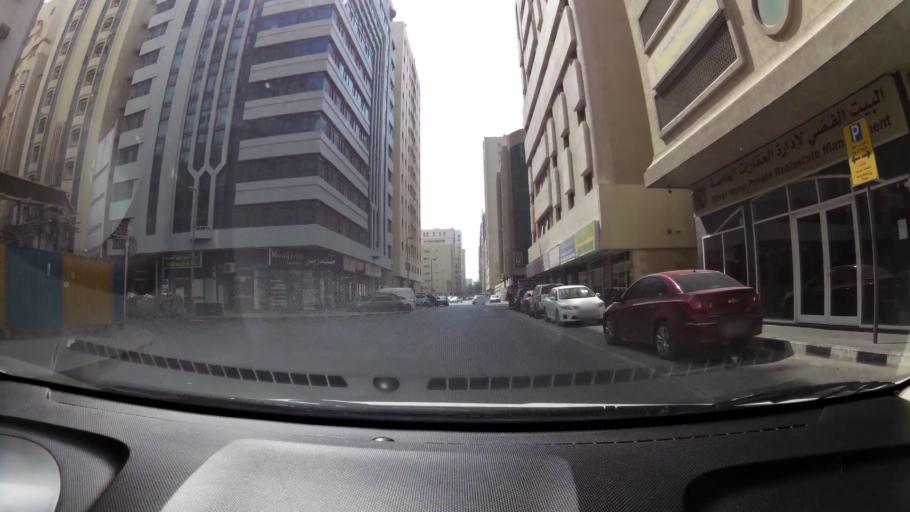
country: AE
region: Ash Shariqah
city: Sharjah
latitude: 25.3484
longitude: 55.3967
